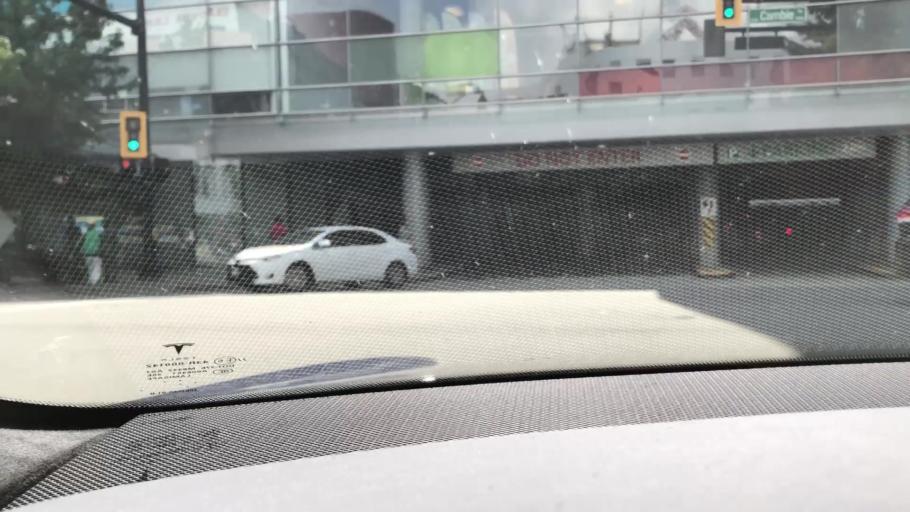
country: CA
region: British Columbia
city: Richmond
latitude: 49.1851
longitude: -123.1344
